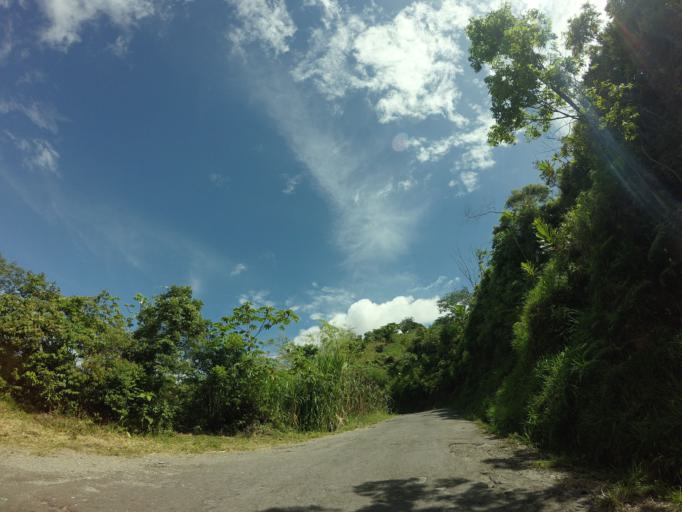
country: CO
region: Caldas
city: Norcasia
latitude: 5.5810
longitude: -74.8766
